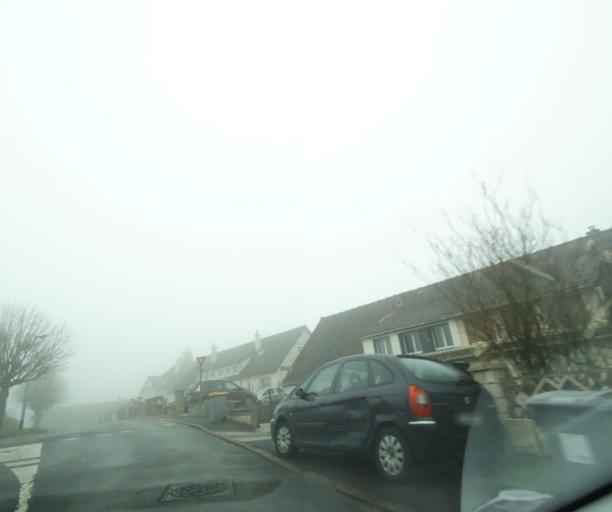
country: FR
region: Ile-de-France
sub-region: Departement de Seine-et-Marne
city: Longperrier
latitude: 49.0533
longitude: 2.6700
